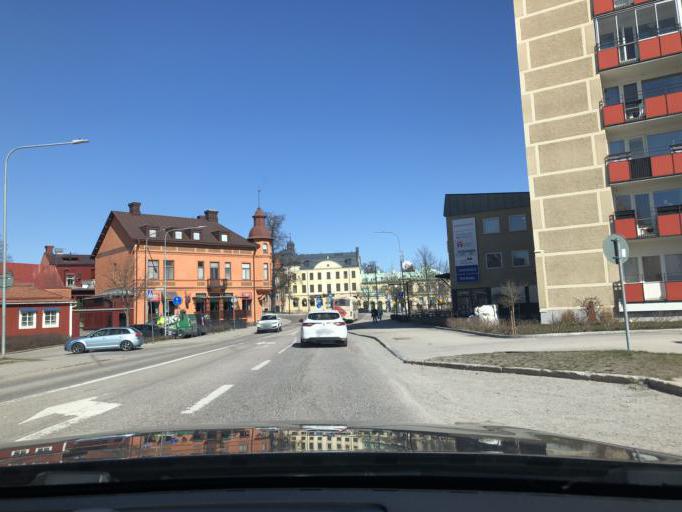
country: SE
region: Gaevleborg
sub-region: Hudiksvalls Kommun
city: Hudiksvall
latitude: 61.7257
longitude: 17.1079
